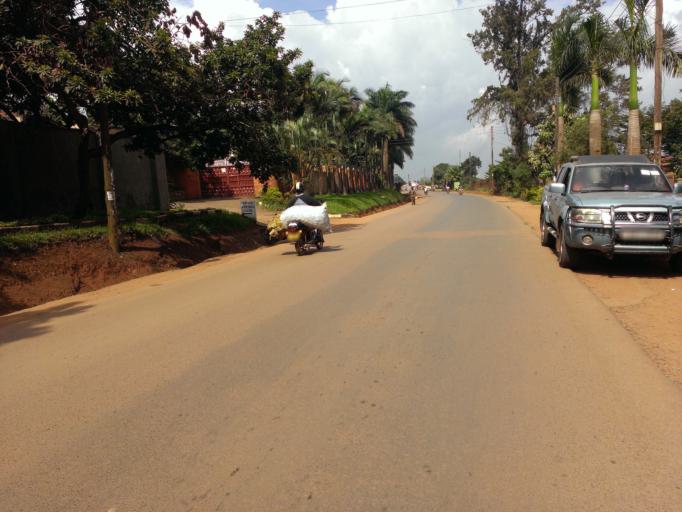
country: UG
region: Central Region
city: Kampala Central Division
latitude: 0.3215
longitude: 32.5590
